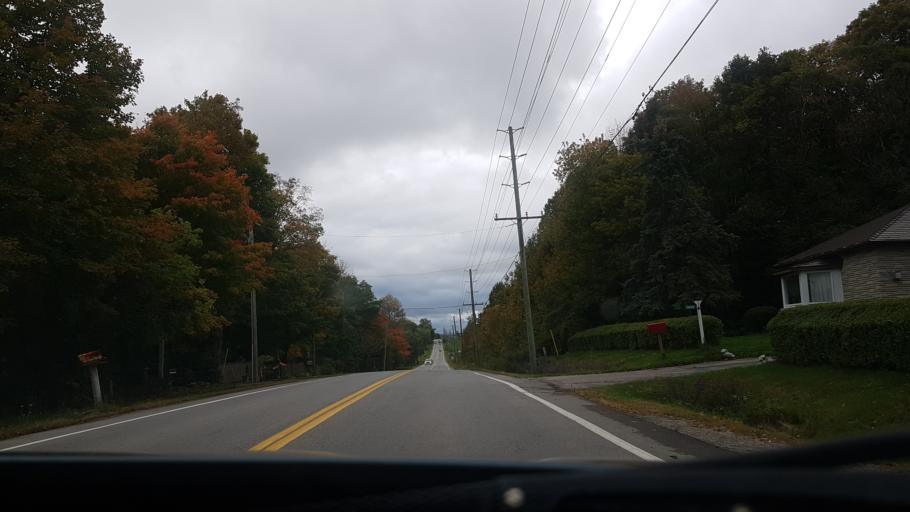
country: CA
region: Ontario
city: Newmarket
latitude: 44.0557
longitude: -79.3905
